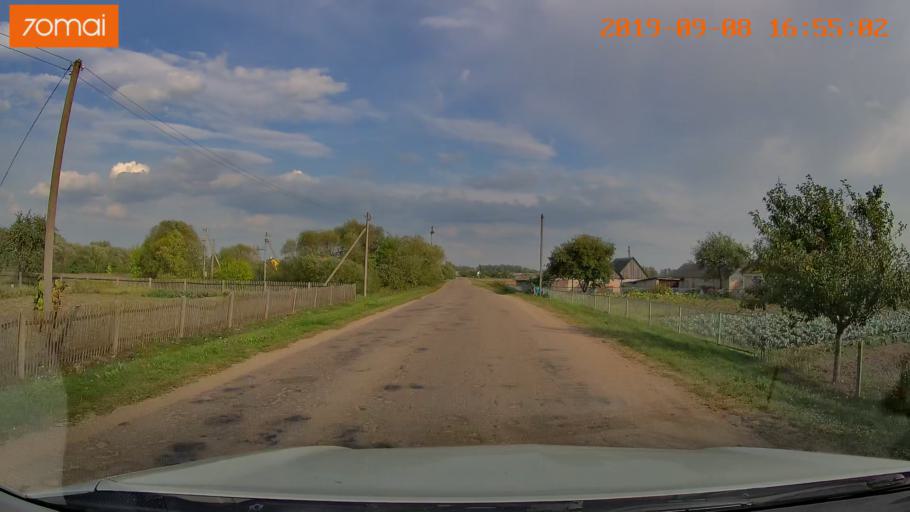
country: BY
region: Grodnenskaya
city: Hrodna
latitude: 53.7490
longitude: 23.9269
